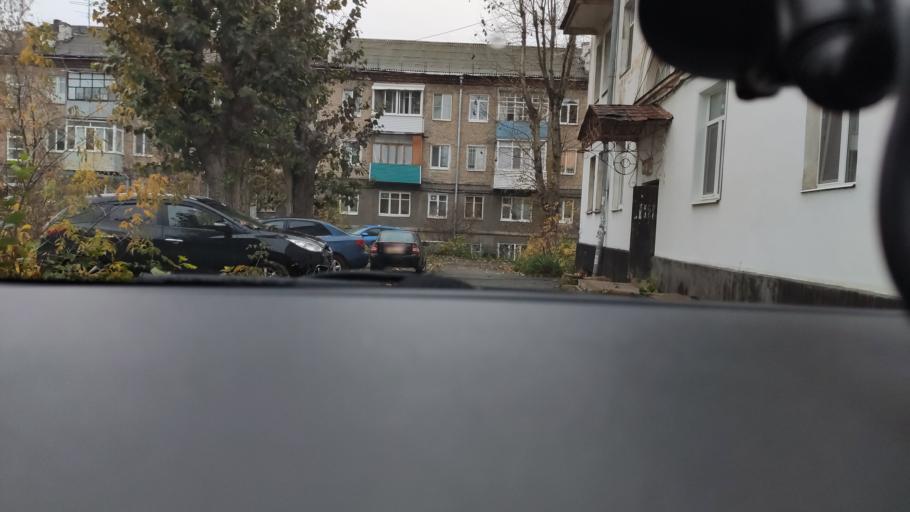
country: RU
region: Perm
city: Perm
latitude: 57.9839
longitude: 56.2124
